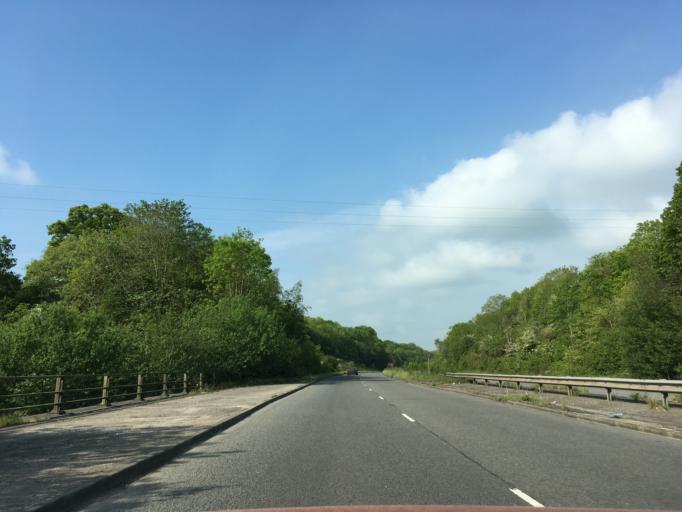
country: GB
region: England
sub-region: North Somerset
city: Long Ashton
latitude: 51.4215
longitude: -2.6580
